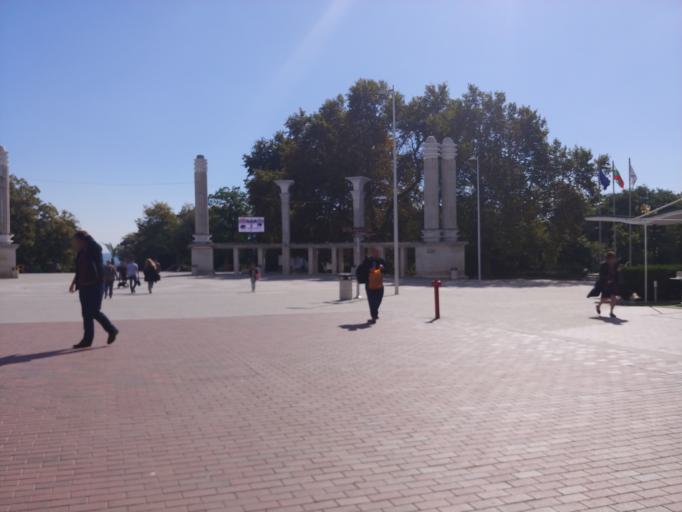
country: BG
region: Varna
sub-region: Obshtina Varna
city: Varna
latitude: 43.2042
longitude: 27.9218
